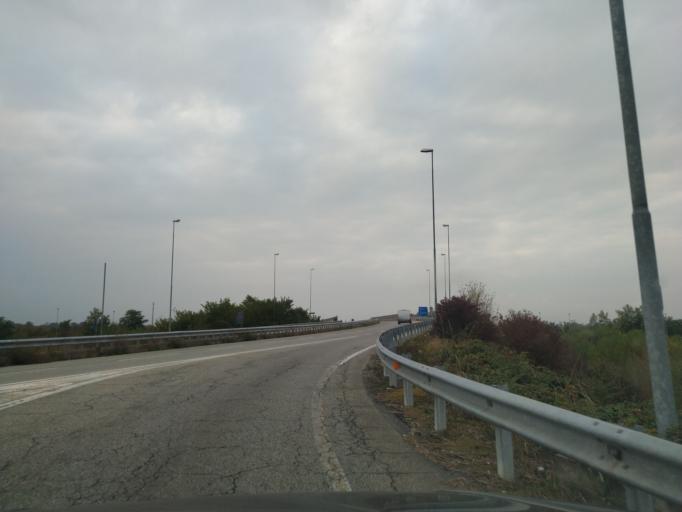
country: IT
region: Piedmont
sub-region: Provincia di Torino
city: Brandizzo
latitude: 45.1858
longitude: 7.8595
